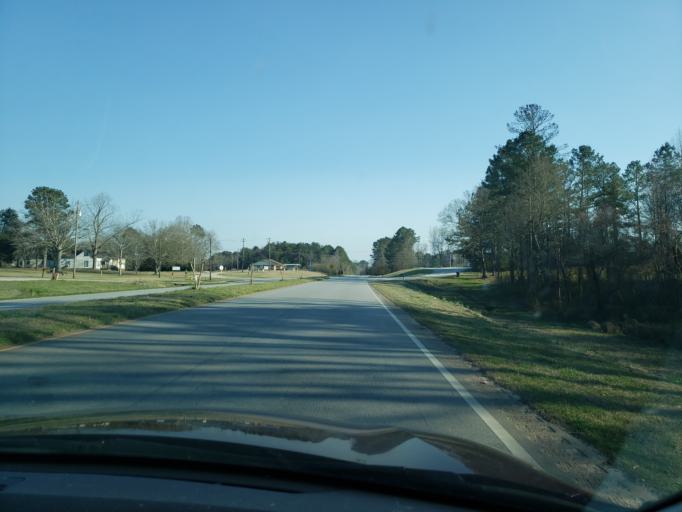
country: US
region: Alabama
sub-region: Randolph County
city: Wedowee
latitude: 33.2911
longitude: -85.4757
